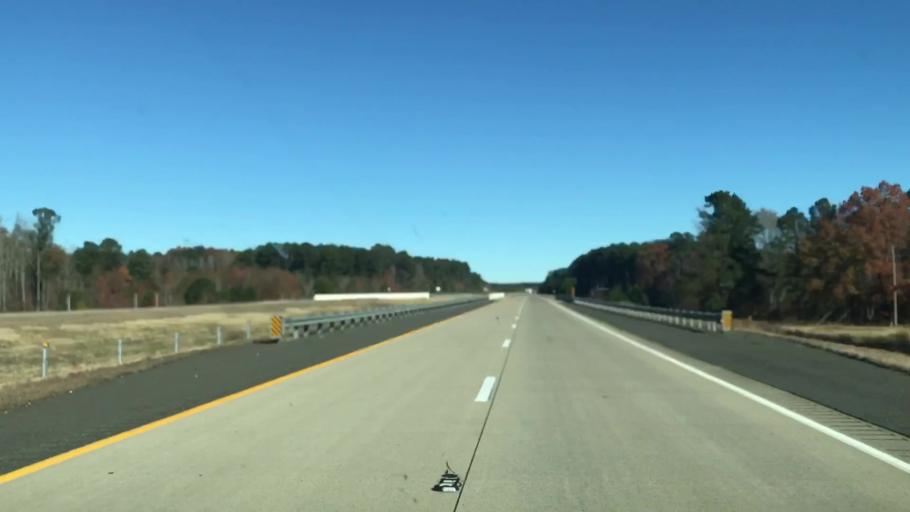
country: US
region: Louisiana
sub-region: Caddo Parish
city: Vivian
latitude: 33.0907
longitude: -93.8946
